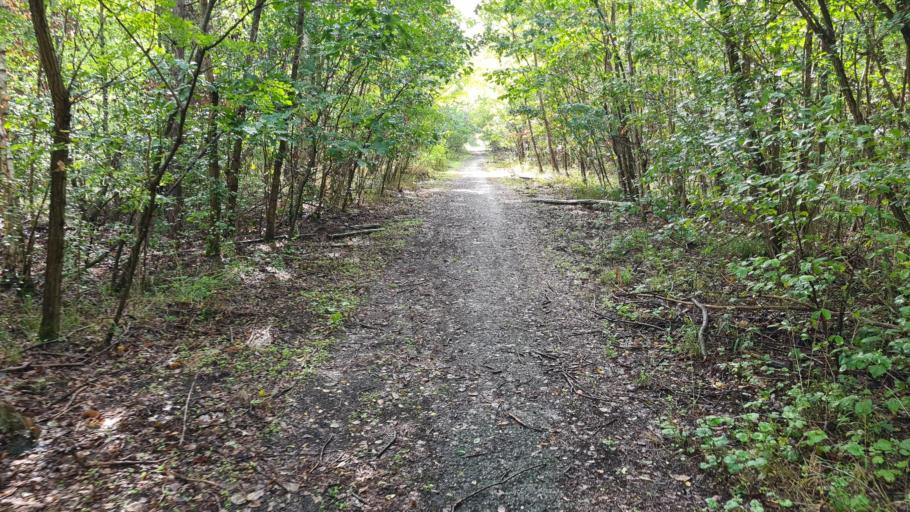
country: DE
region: Brandenburg
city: Sallgast
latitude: 51.5634
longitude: 13.8581
